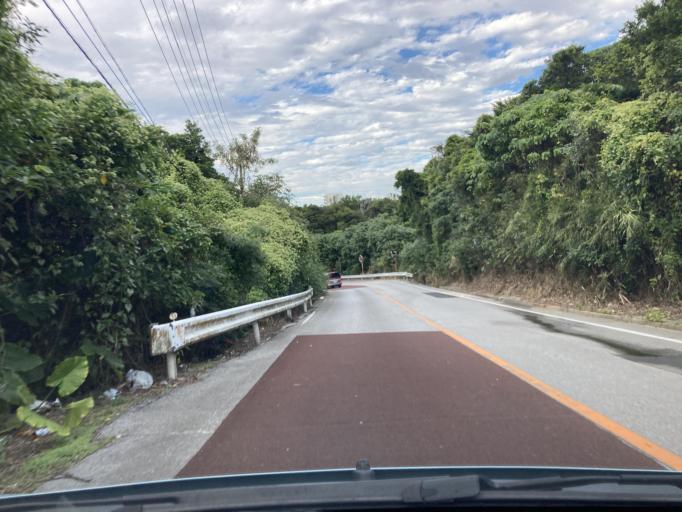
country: JP
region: Okinawa
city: Ishikawa
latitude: 26.4371
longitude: 127.8053
